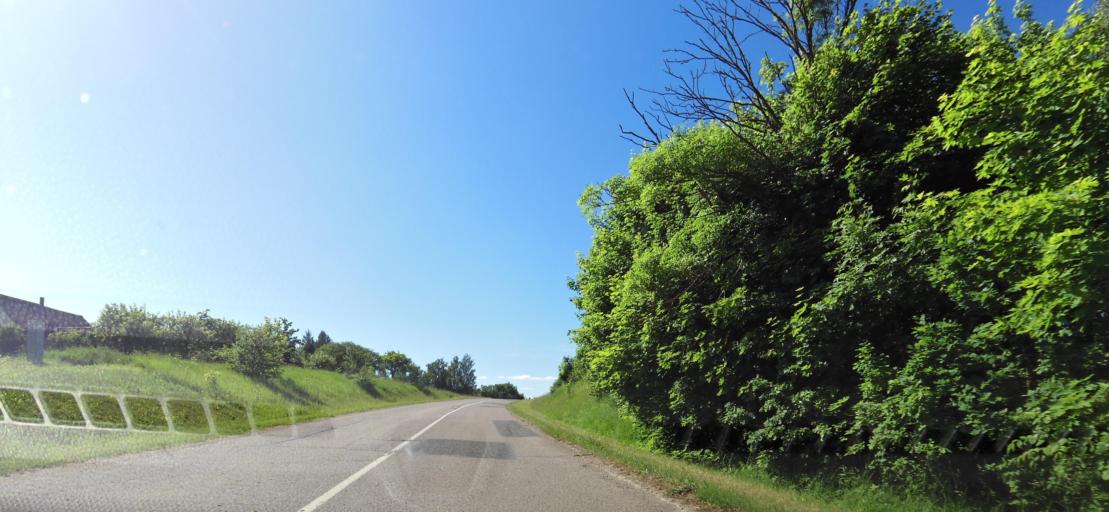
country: LT
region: Utenos apskritis
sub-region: Anyksciai
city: Anyksciai
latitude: 55.3910
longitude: 25.0822
